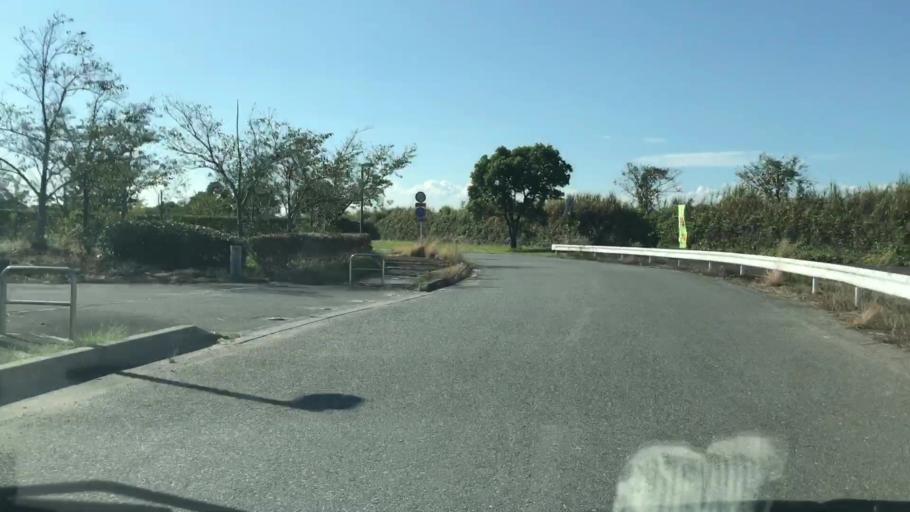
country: JP
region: Saga Prefecture
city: Okawa
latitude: 33.1523
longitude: 130.3110
